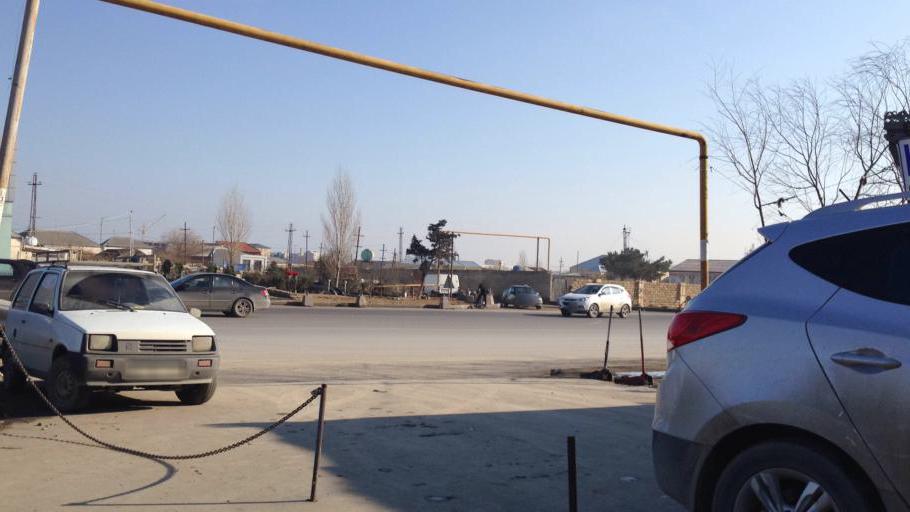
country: AZ
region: Baki
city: Sabuncu
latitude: 40.4461
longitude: 49.9341
